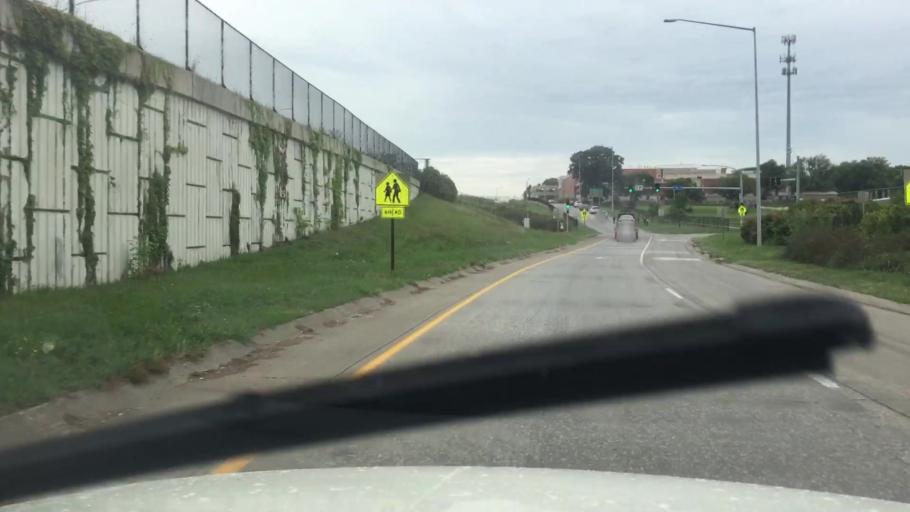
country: US
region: Iowa
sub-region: Polk County
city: Des Moines
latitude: 41.5972
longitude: -93.5951
